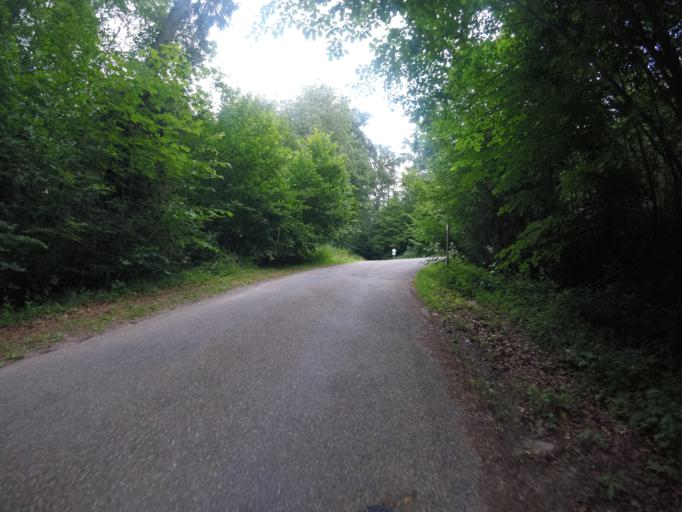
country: DE
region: Baden-Wuerttemberg
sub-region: Regierungsbezirk Stuttgart
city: Oppenweiler
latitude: 48.9841
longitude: 9.4759
